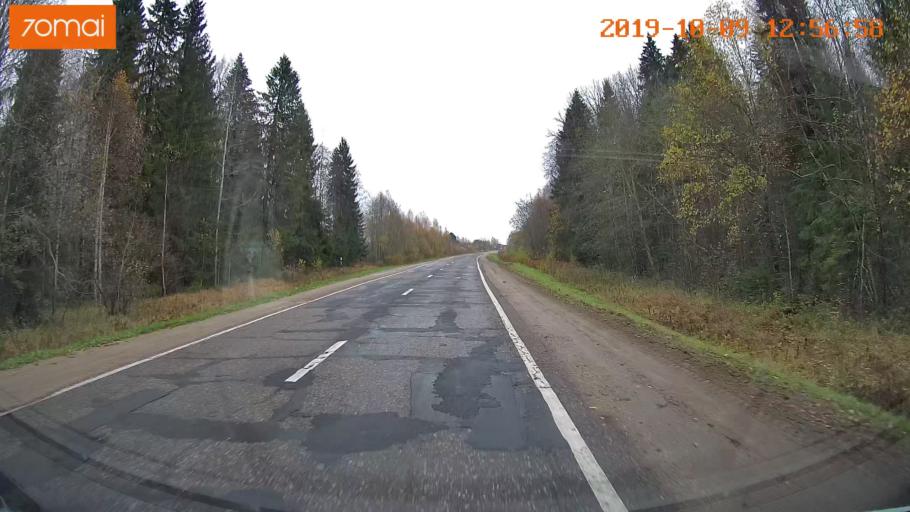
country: RU
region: Jaroslavl
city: Prechistoye
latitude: 58.3937
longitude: 40.4254
